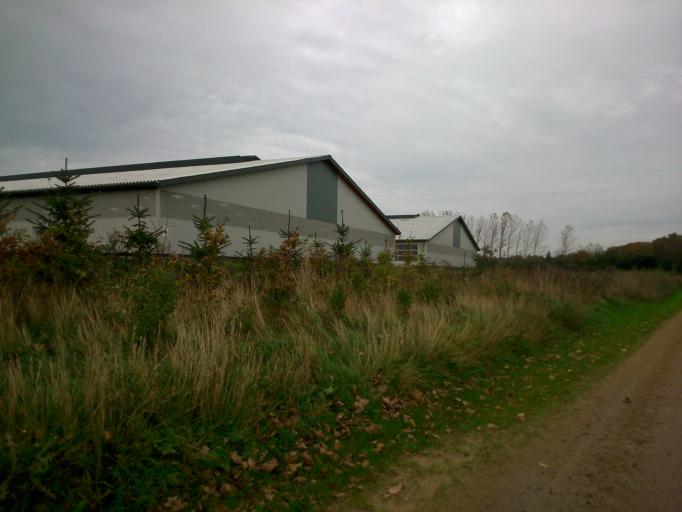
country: DK
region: Central Jutland
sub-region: Ringkobing-Skjern Kommune
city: Skjern
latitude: 55.9738
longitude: 8.5042
